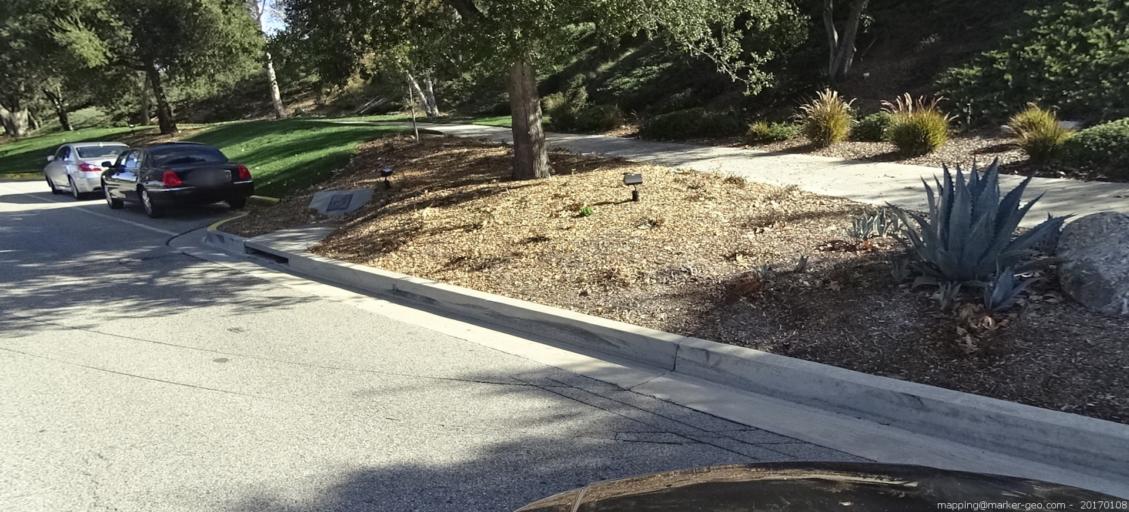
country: US
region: California
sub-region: Orange County
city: Coto De Caza
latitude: 33.5723
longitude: -117.5916
